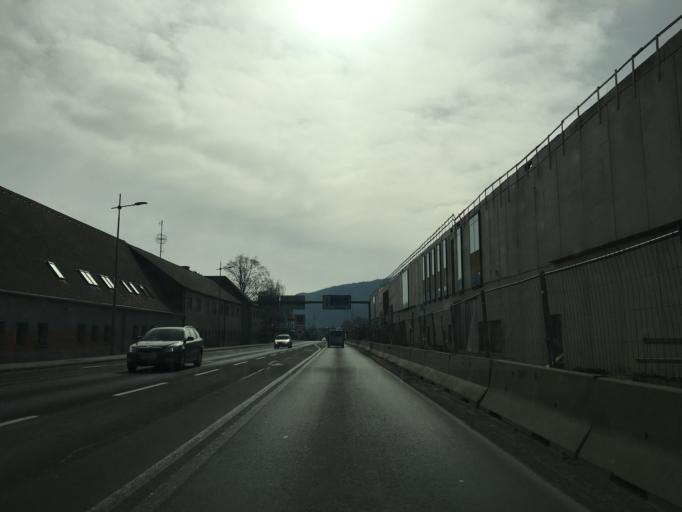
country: AT
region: Styria
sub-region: Politischer Bezirk Liezen
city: Liezen
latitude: 47.5625
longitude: 14.2446
